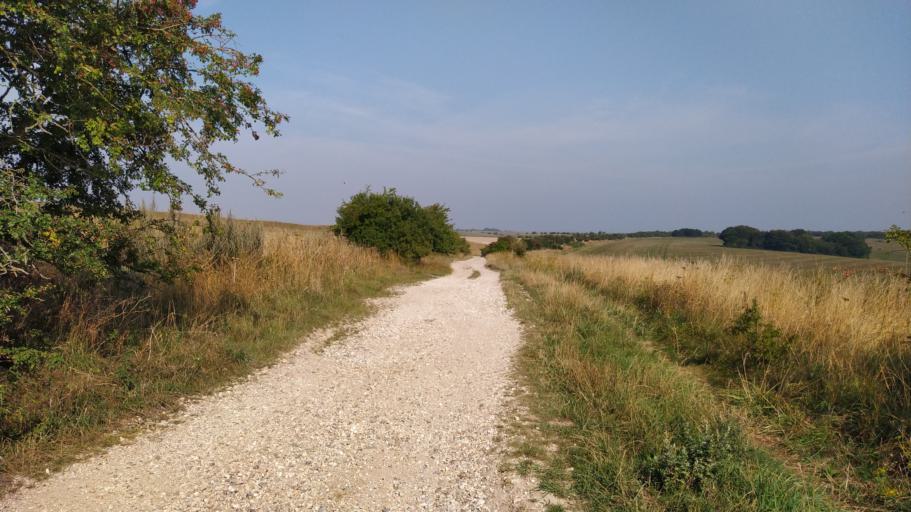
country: GB
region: England
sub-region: Wiltshire
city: Winterbourne Stoke
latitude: 51.1628
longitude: -1.9463
